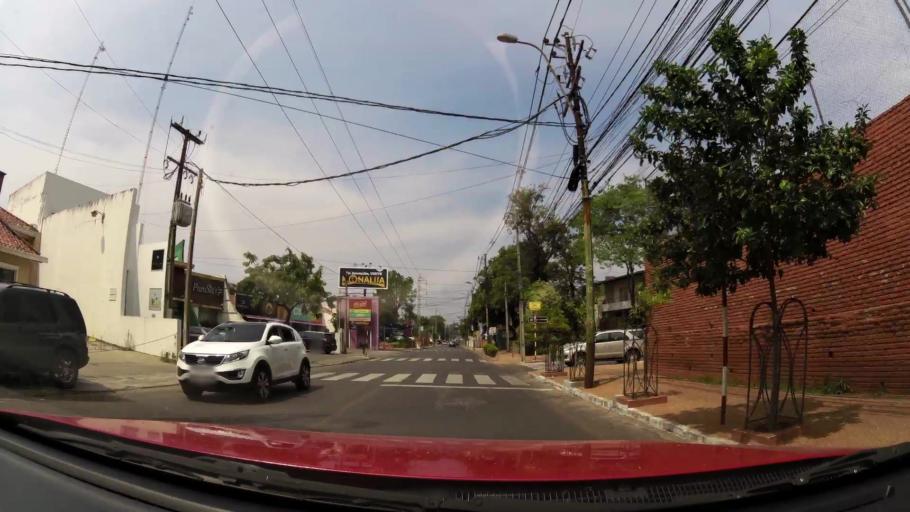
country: PY
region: Asuncion
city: Asuncion
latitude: -25.2871
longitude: -57.5938
